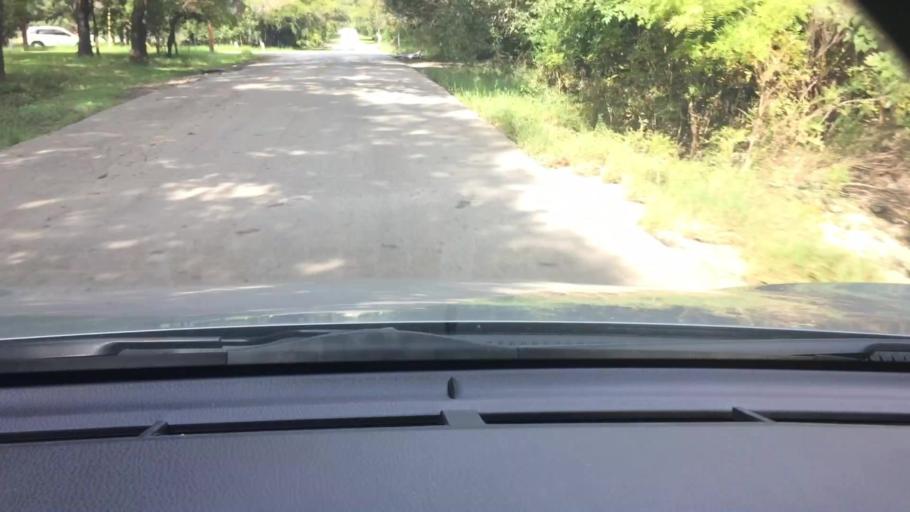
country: US
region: Texas
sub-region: Bexar County
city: Shavano Park
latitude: 29.5525
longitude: -98.5638
